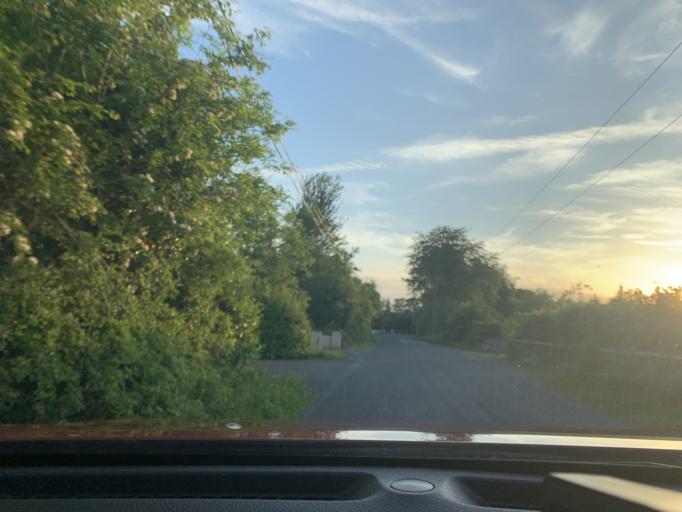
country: IE
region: Connaught
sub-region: Sligo
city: Sligo
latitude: 54.2912
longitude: -8.4347
